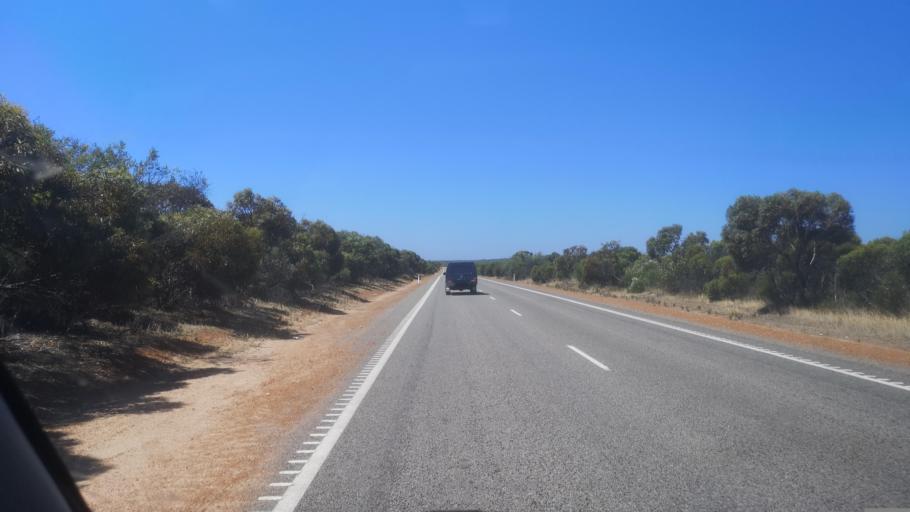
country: AU
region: Western Australia
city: Port Denison
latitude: -29.5313
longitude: 114.9940
